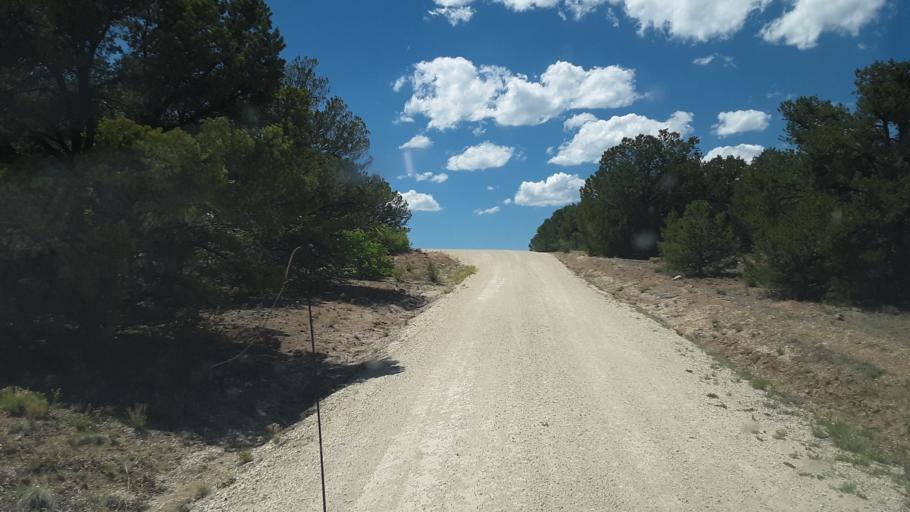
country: US
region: Colorado
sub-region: Custer County
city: Westcliffe
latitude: 38.3281
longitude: -105.6334
